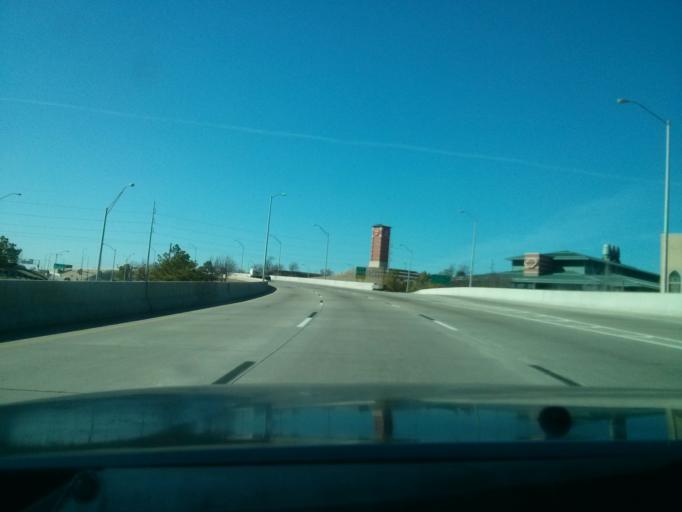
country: US
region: Oklahoma
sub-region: Tulsa County
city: Tulsa
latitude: 36.1621
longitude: -95.9895
